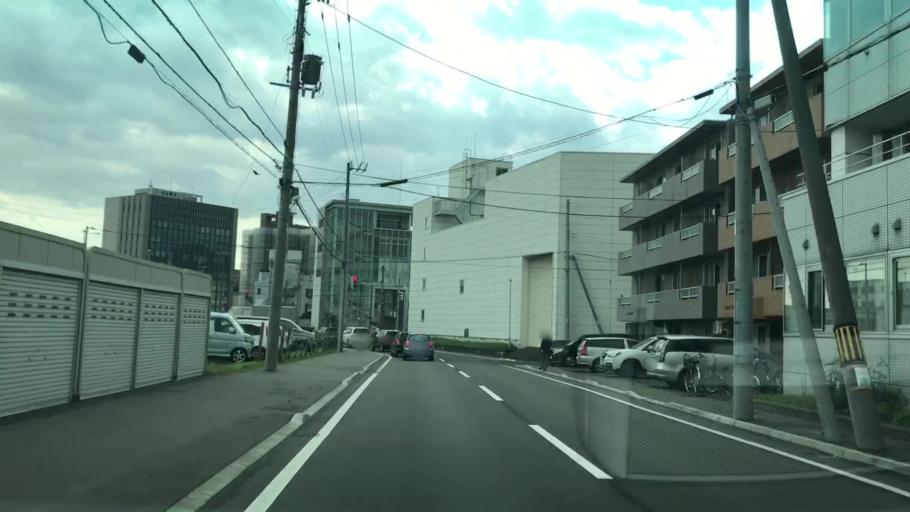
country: JP
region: Hokkaido
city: Sapporo
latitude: 43.0708
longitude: 141.3163
